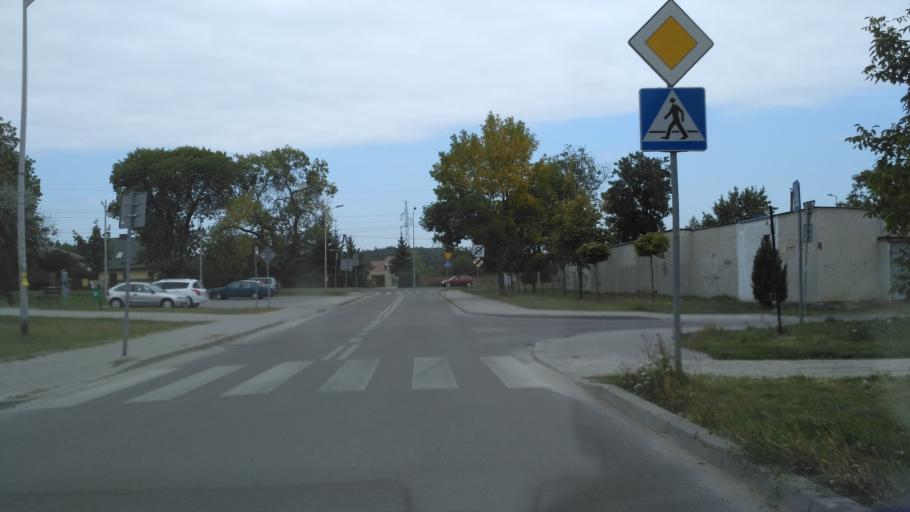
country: PL
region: Lublin Voivodeship
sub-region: Chelm
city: Chelm
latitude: 51.1437
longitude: 23.4308
